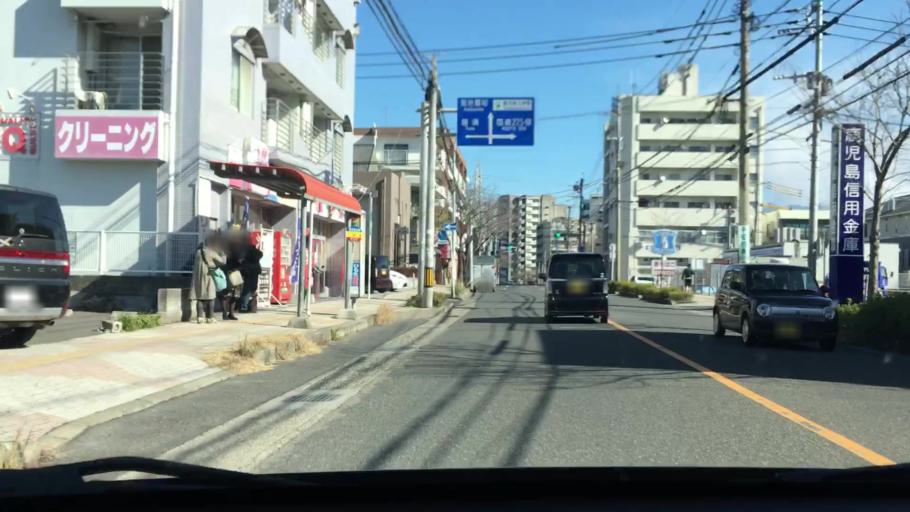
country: JP
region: Kagoshima
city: Kagoshima-shi
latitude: 31.5620
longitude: 130.5344
